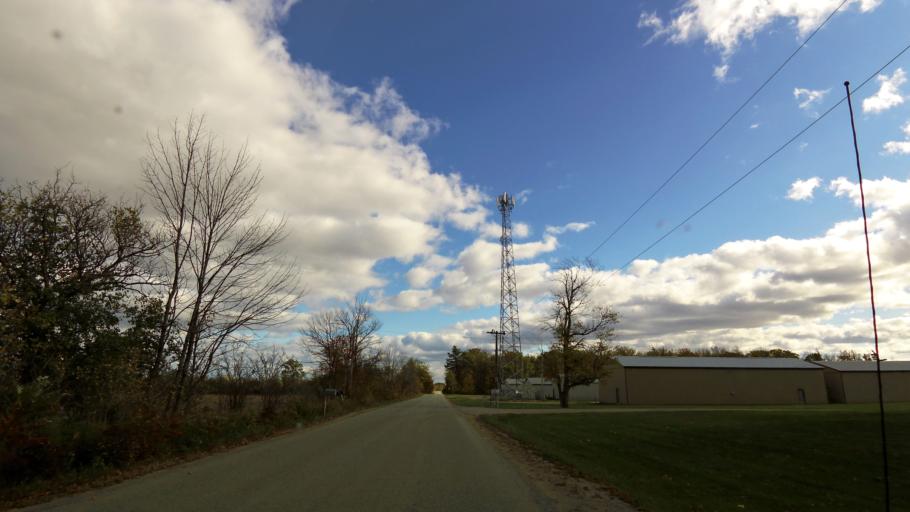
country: CA
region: Ontario
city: Burlington
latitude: 43.4468
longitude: -79.8520
